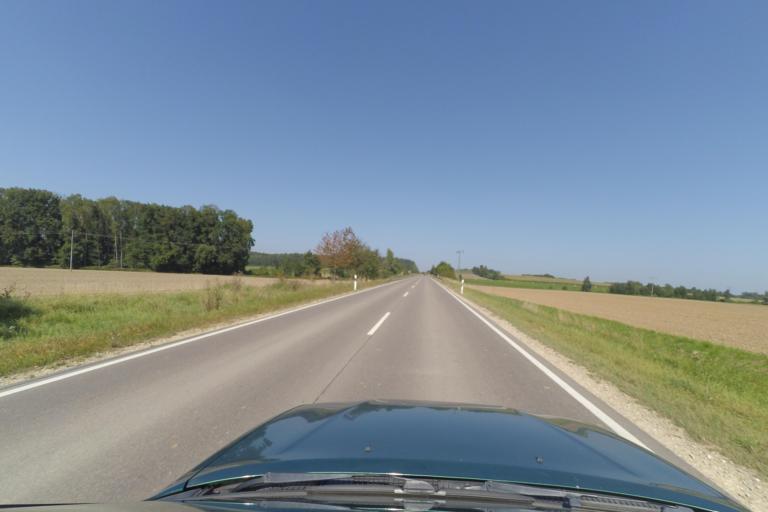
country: DE
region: Bavaria
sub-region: Swabia
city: Wittislingen
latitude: 48.6091
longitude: 10.4068
